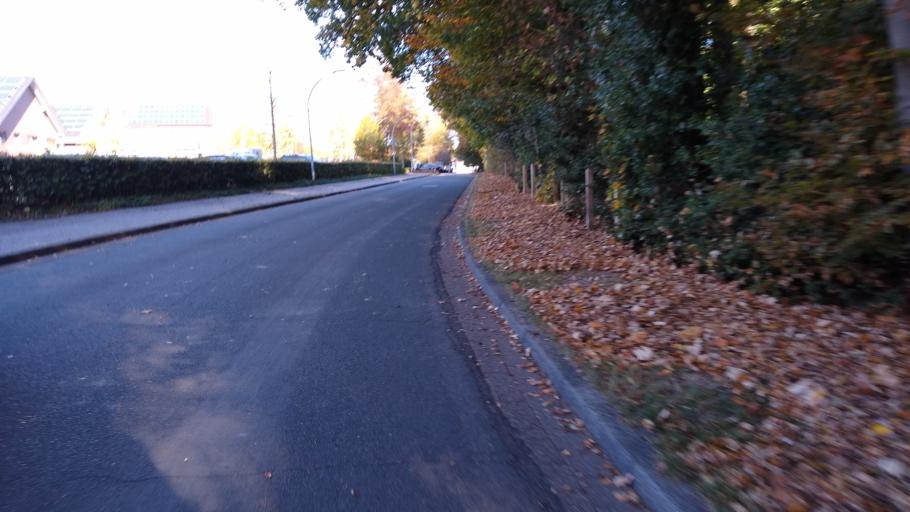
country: DE
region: Lower Saxony
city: Rastede
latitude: 53.2401
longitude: 8.1961
